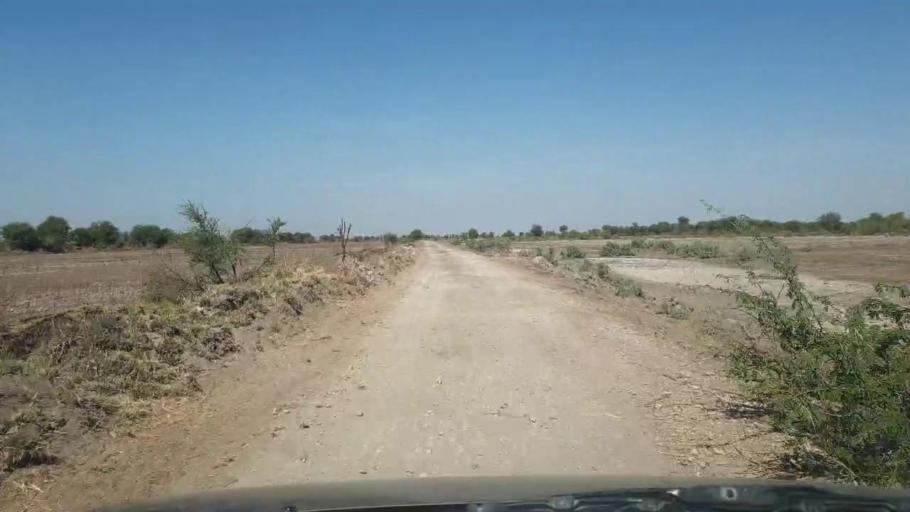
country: PK
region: Sindh
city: Dhoro Naro
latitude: 25.4299
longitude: 69.6200
